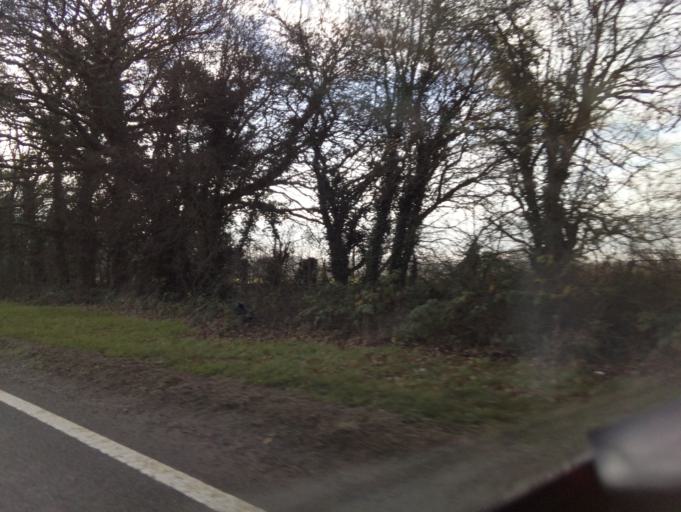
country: GB
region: England
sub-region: Warwickshire
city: Curdworth
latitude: 52.5735
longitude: -1.7665
